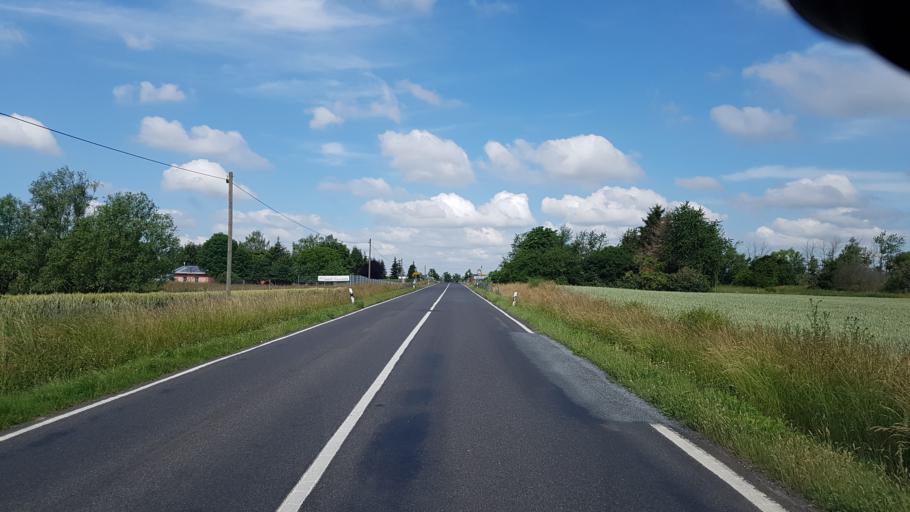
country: DE
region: Mecklenburg-Vorpommern
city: Strasburg
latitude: 53.4246
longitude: 13.6974
